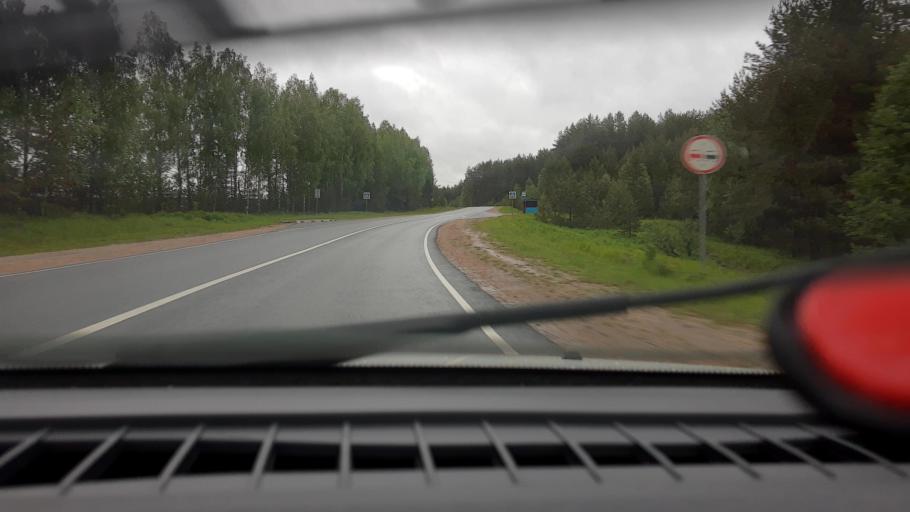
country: RU
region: Nizjnij Novgorod
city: Krasnyye Baki
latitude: 57.0300
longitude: 45.1162
